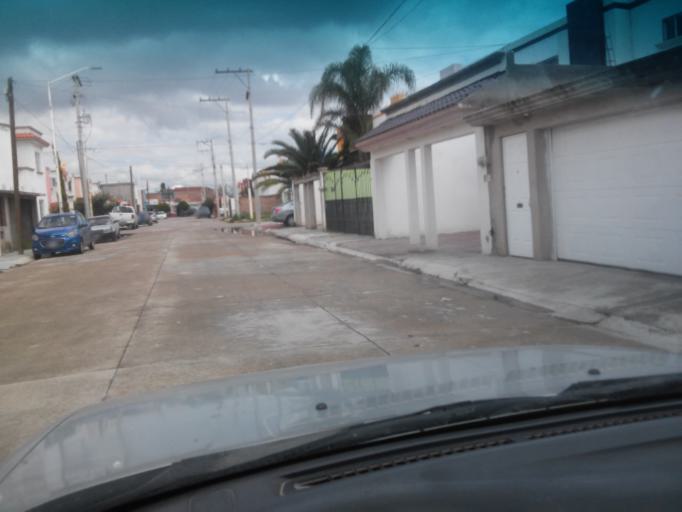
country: MX
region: Durango
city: Victoria de Durango
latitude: 24.0056
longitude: -104.6355
